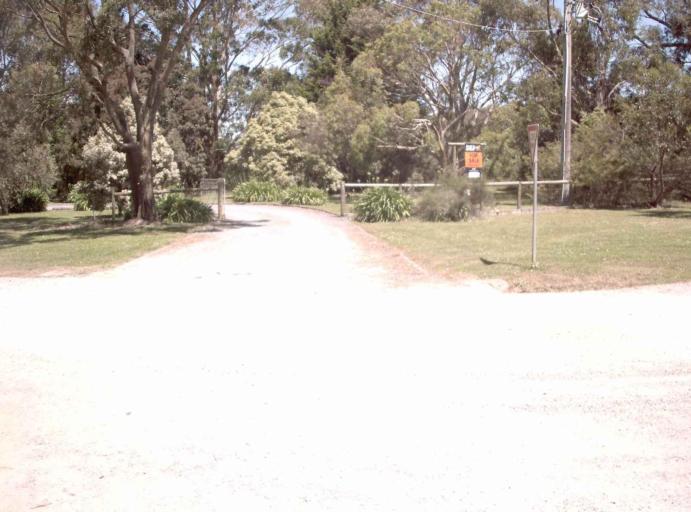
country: AU
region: Victoria
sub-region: Bass Coast
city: North Wonthaggi
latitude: -38.7562
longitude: 146.0728
